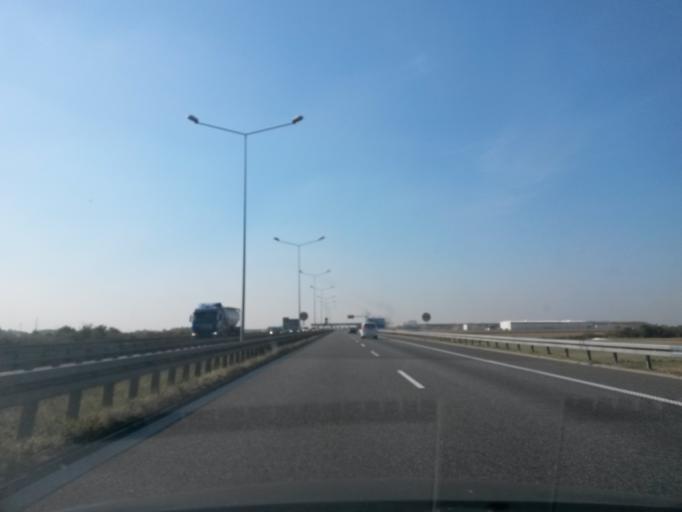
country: PL
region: Silesian Voivodeship
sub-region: Gliwice
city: Gliwice
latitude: 50.2590
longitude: 18.6831
